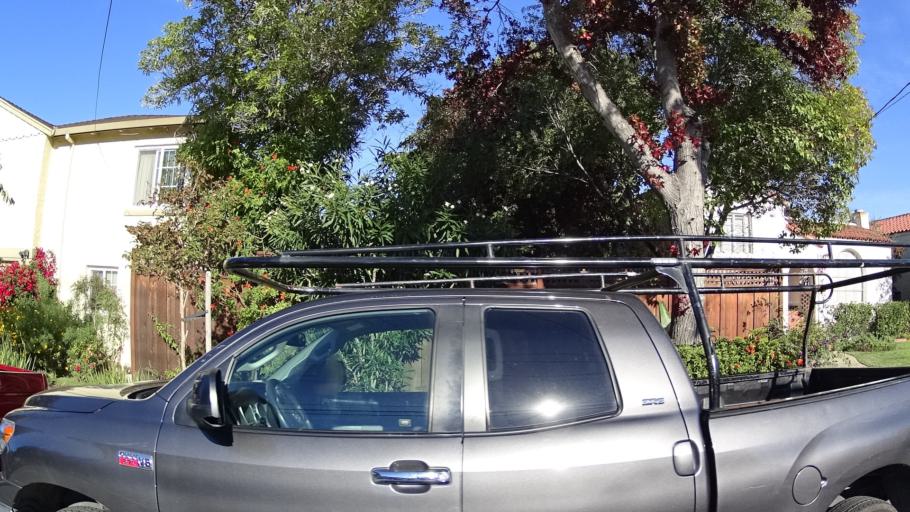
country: US
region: California
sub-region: San Mateo County
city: San Mateo
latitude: 37.5827
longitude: -122.3405
